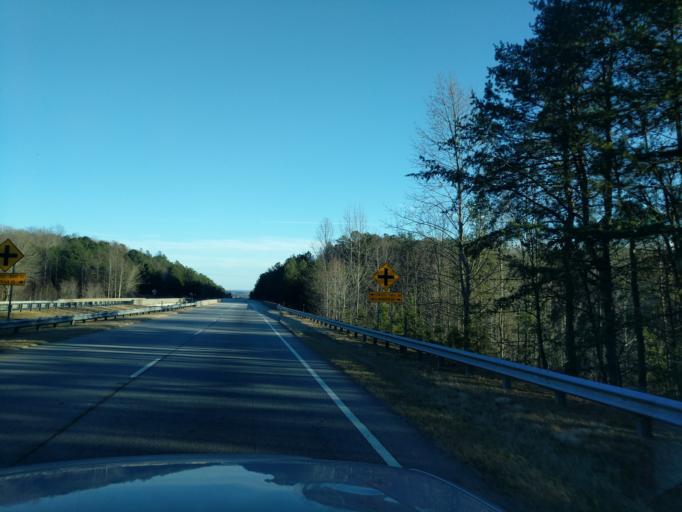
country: US
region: Georgia
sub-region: Stephens County
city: Toccoa
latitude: 34.5631
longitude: -83.3948
